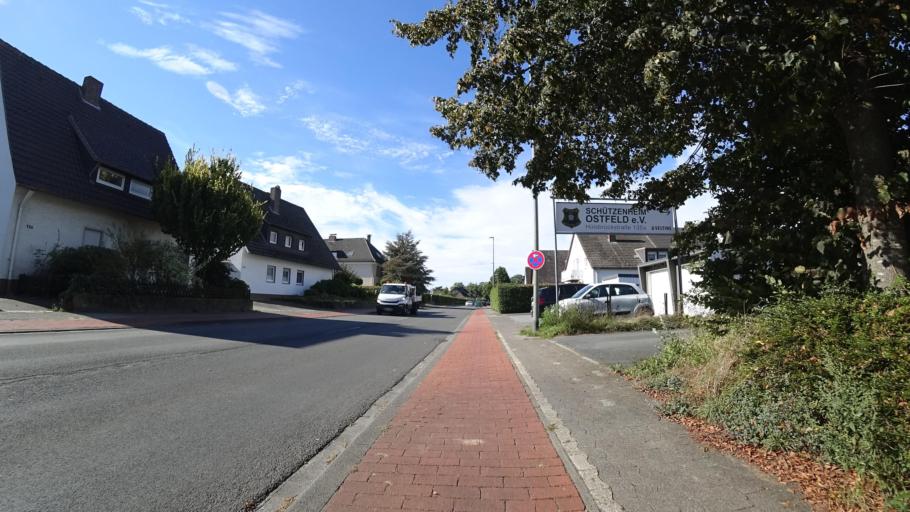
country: DE
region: North Rhine-Westphalia
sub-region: Regierungsbezirk Detmold
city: Guetersloh
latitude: 51.9186
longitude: 8.4169
